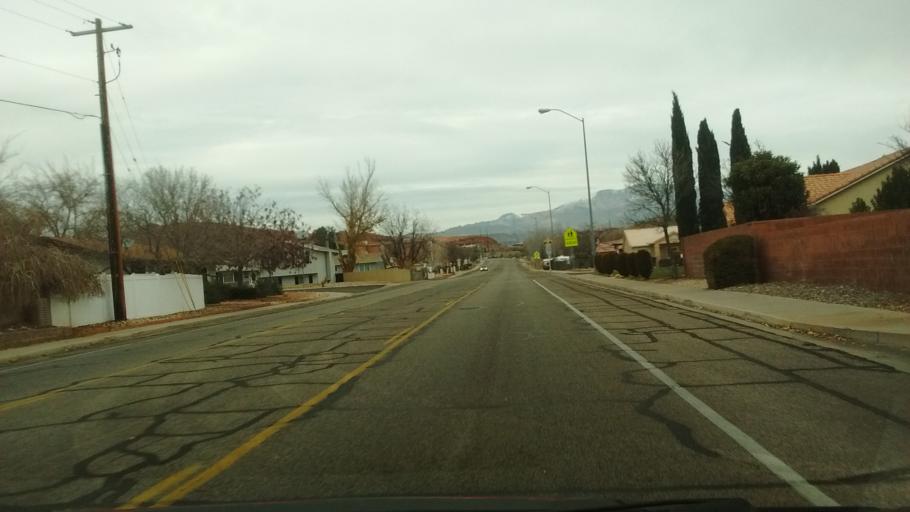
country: US
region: Utah
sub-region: Washington County
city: Washington
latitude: 37.1199
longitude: -113.5317
